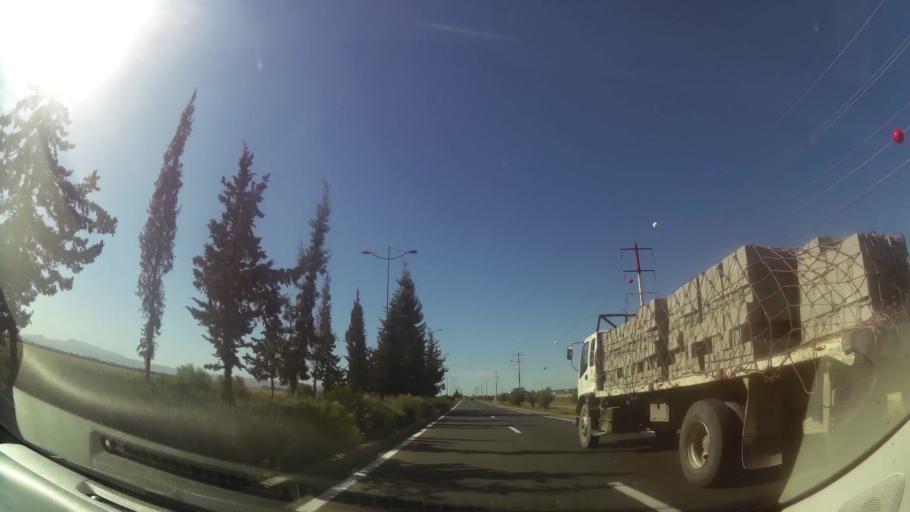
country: MA
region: Oriental
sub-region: Oujda-Angad
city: Oujda
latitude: 34.7599
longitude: -1.9376
